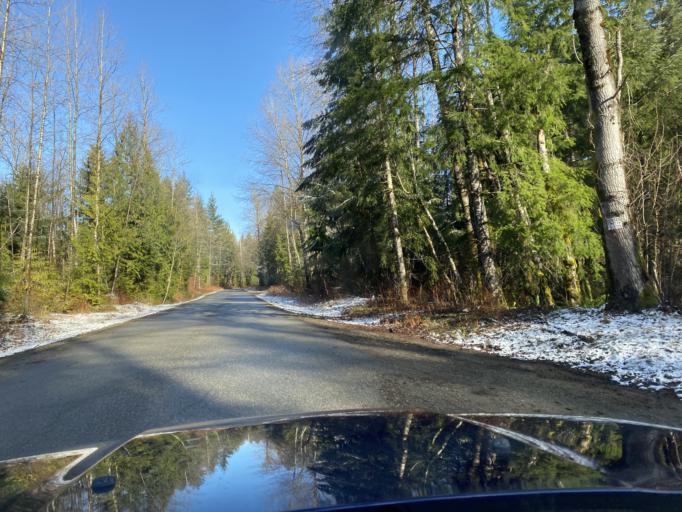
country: US
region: Washington
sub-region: King County
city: Snoqualmie
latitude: 47.5053
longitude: -121.8829
